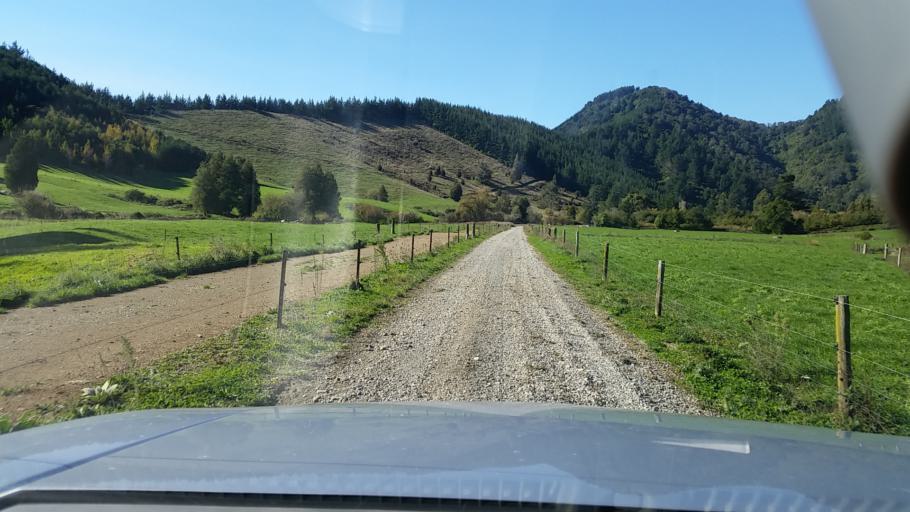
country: NZ
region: Nelson
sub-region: Nelson City
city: Nelson
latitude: -41.2220
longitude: 173.6071
